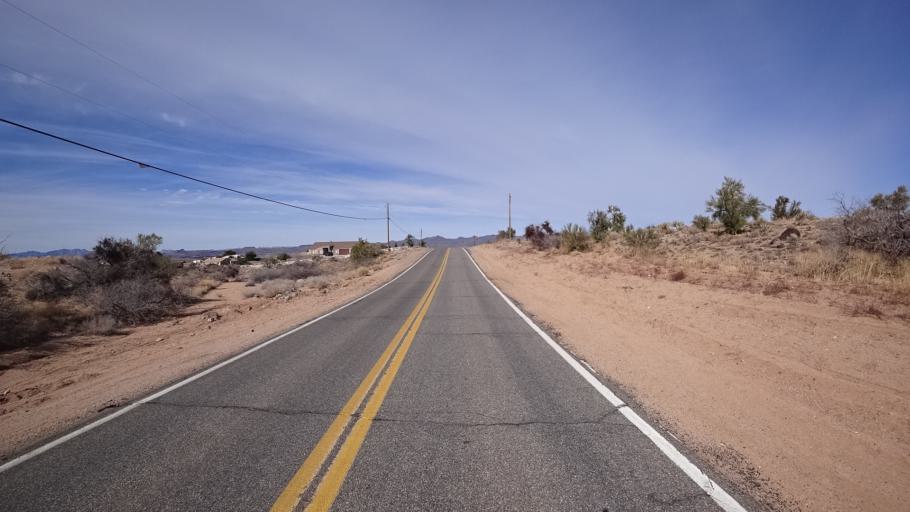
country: US
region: Arizona
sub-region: Mohave County
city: Kingman
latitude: 35.1709
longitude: -113.9808
